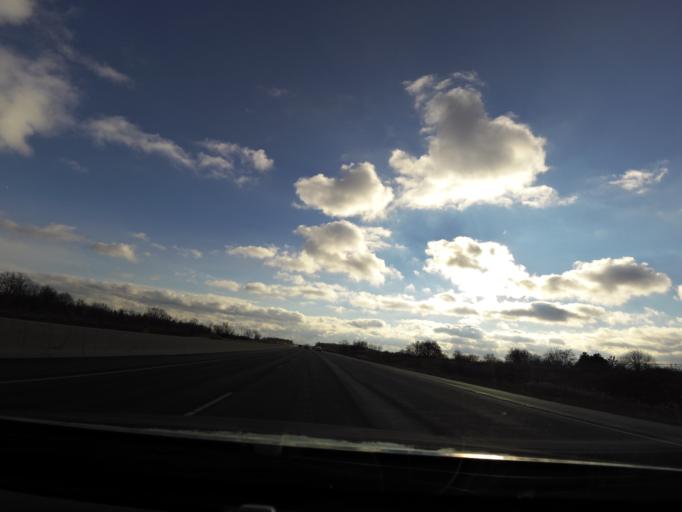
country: CA
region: Ontario
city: Burlington
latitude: 43.4646
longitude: -79.7853
